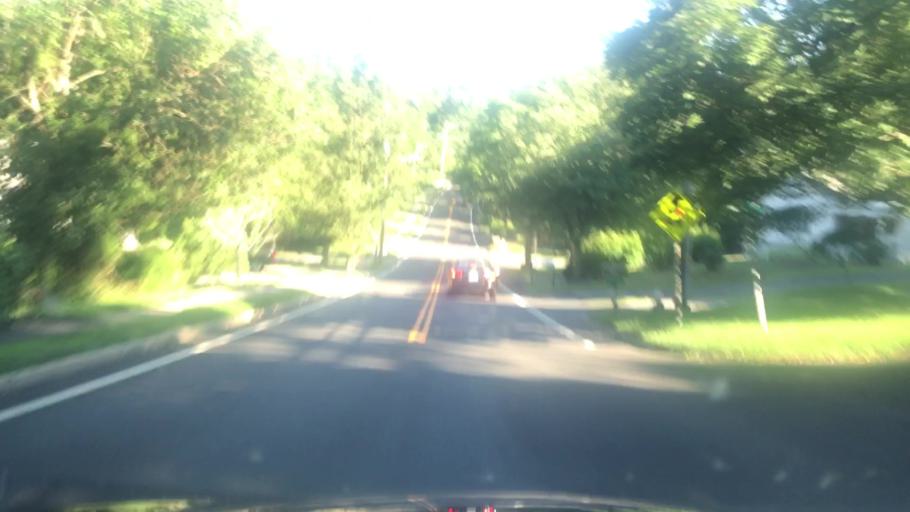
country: US
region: Connecticut
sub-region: Fairfield County
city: Glenville
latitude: 41.0337
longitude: -73.6586
